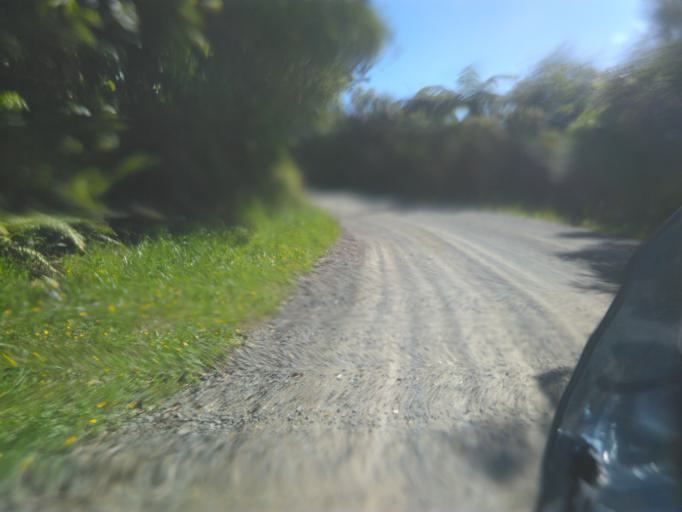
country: NZ
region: Hawke's Bay
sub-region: Wairoa District
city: Wairoa
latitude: -38.7973
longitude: 177.1252
